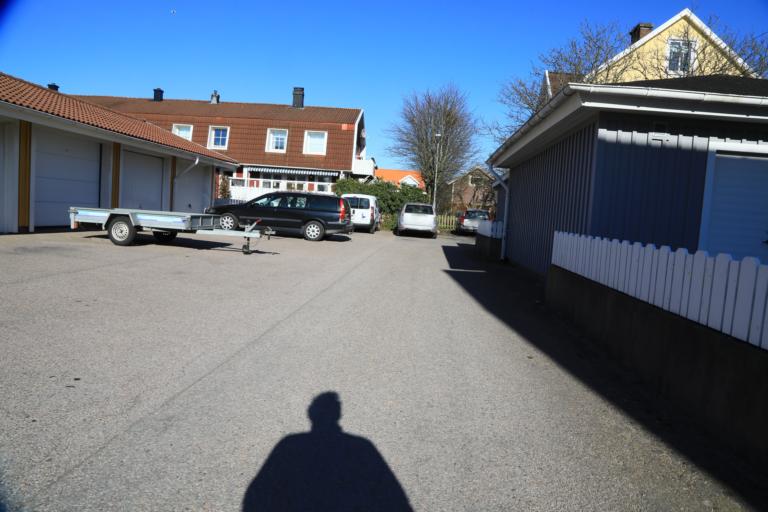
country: SE
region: Halland
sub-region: Varbergs Kommun
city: Varberg
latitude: 57.0977
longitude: 12.2513
